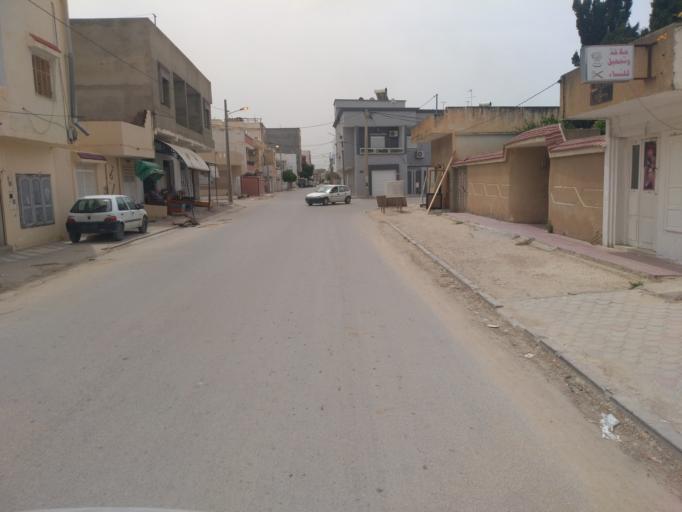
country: TN
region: Al Qayrawan
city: Kairouan
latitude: 35.6687
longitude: 10.0828
